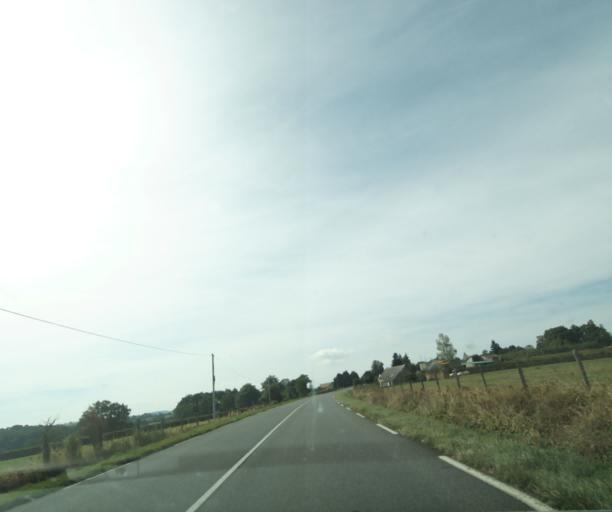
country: FR
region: Auvergne
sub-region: Departement de l'Allier
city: Le Donjon
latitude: 46.3333
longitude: 3.7724
